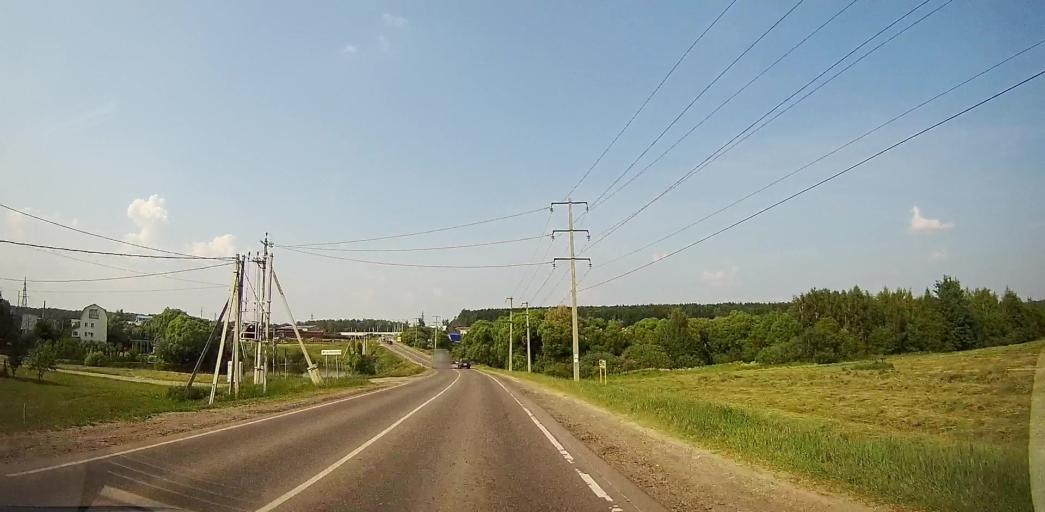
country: RU
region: Moskovskaya
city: Barybino
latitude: 55.2742
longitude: 37.9161
